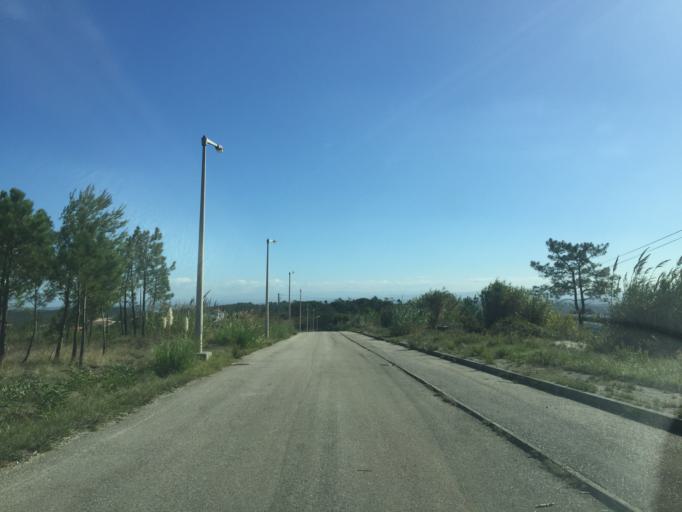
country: PT
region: Coimbra
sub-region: Figueira da Foz
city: Tavarede
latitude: 40.1902
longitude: -8.8334
